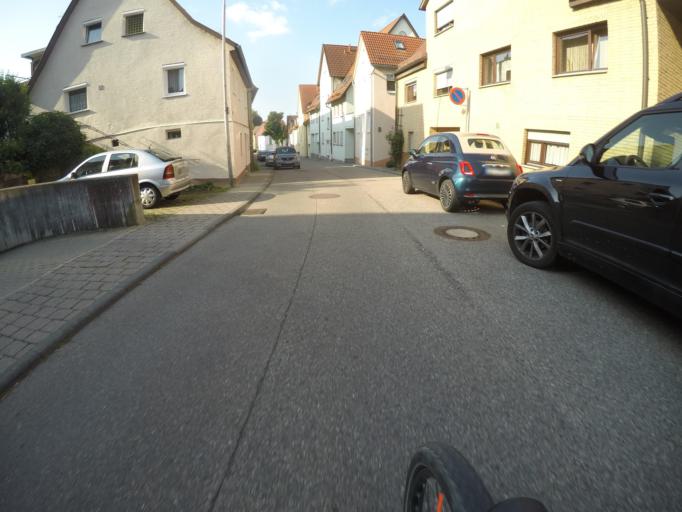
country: DE
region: Baden-Wuerttemberg
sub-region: Regierungsbezirk Stuttgart
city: Herrenberg
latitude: 48.5740
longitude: 8.8772
